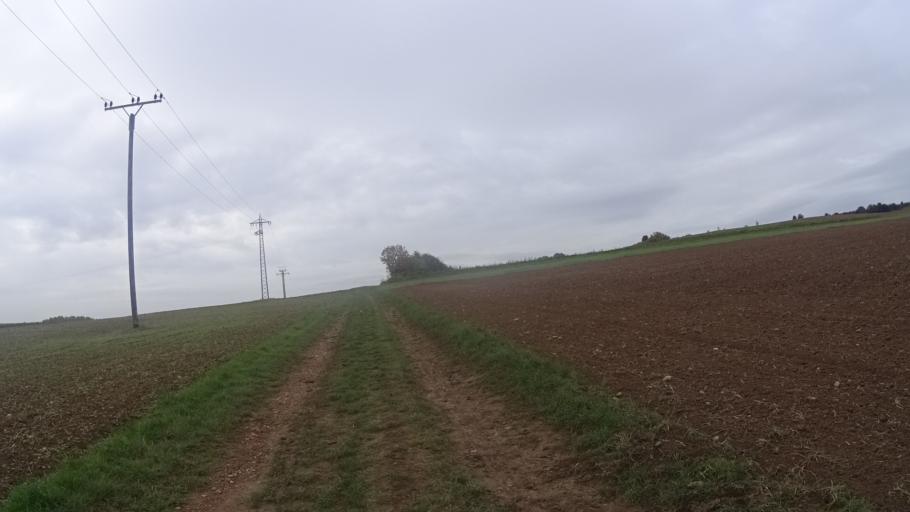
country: DE
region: Rheinland-Pfalz
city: Bubenheim
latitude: 49.6305
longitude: 8.1145
